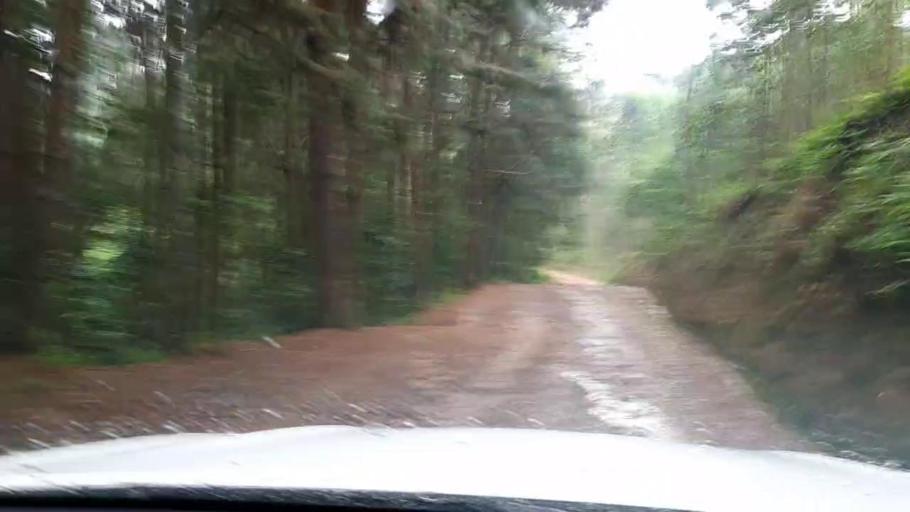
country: RW
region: Western Province
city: Cyangugu
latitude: -2.5551
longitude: 28.9782
